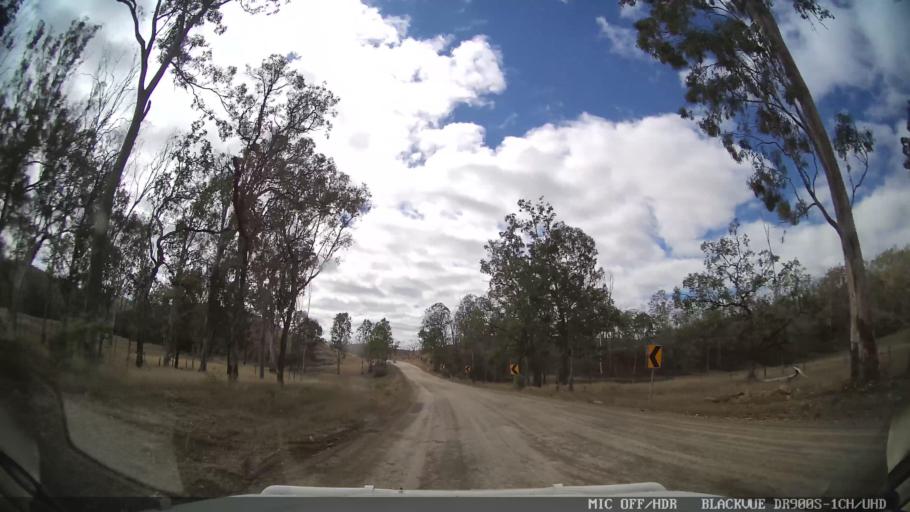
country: AU
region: Queensland
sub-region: Gladstone
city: Toolooa
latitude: -24.6195
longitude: 151.2971
